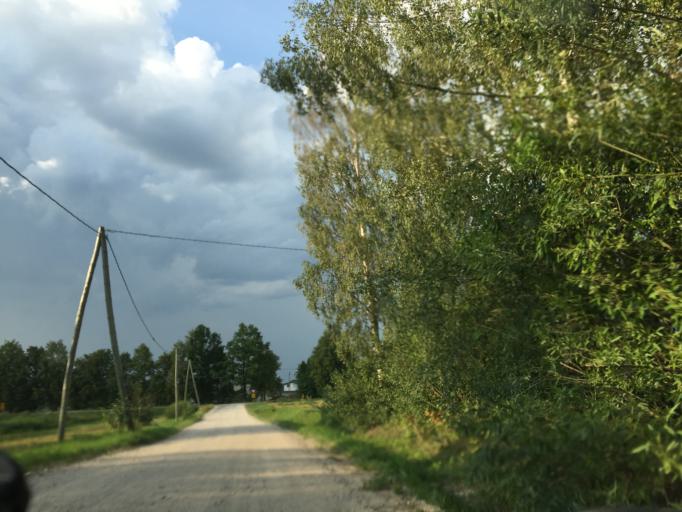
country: LV
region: Dobeles Rajons
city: Dobele
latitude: 56.5962
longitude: 23.3105
